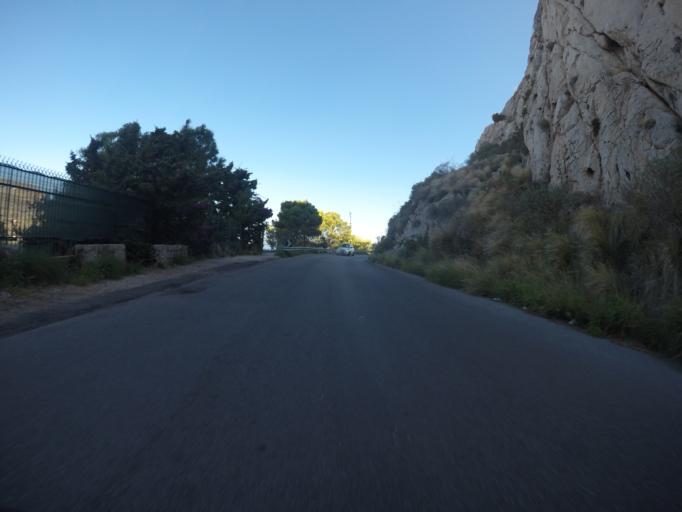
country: IT
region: Sicily
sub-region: Palermo
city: Palermo
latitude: 38.1945
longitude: 13.3379
